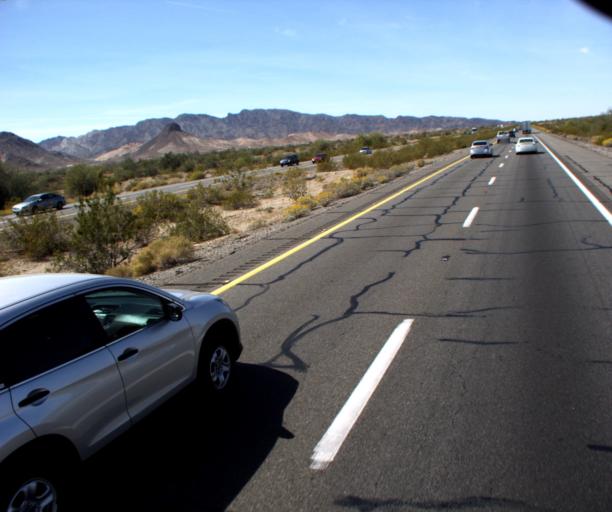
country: US
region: Arizona
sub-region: La Paz County
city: Quartzsite
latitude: 33.6529
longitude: -114.2904
